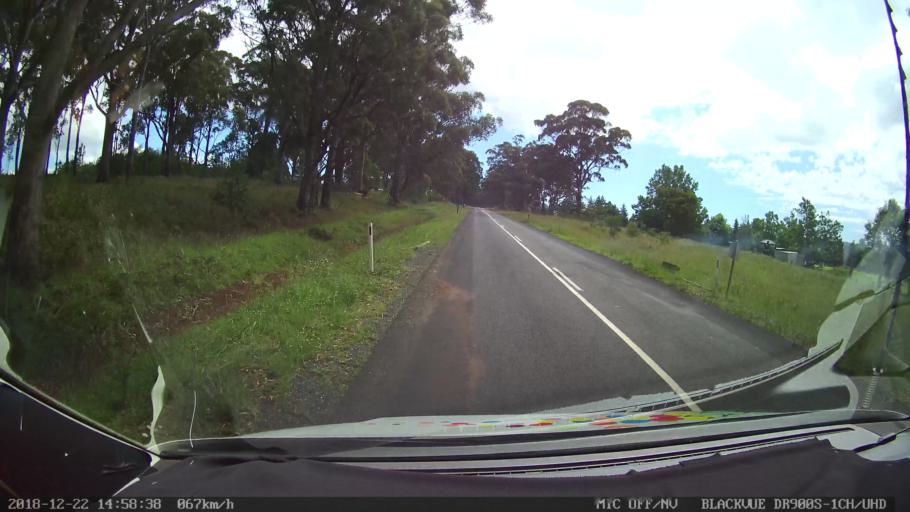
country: AU
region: New South Wales
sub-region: Bellingen
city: Dorrigo
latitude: -30.2414
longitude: 152.4891
